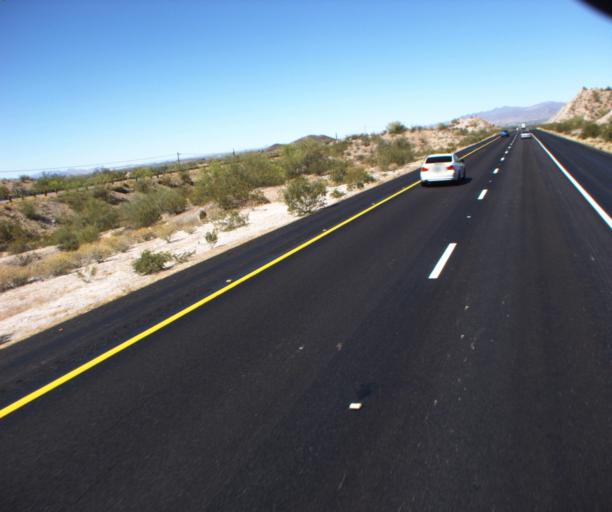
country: US
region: Arizona
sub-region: Maricopa County
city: Buckeye
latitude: 33.2965
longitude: -112.6275
